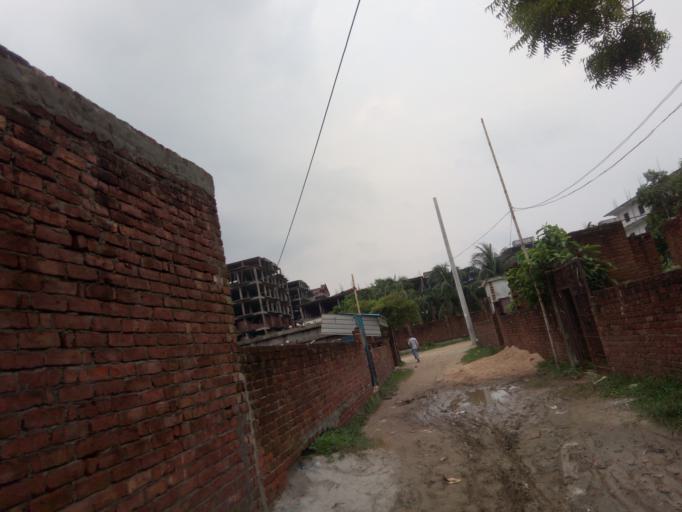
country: BD
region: Dhaka
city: Azimpur
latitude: 23.7421
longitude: 90.3564
